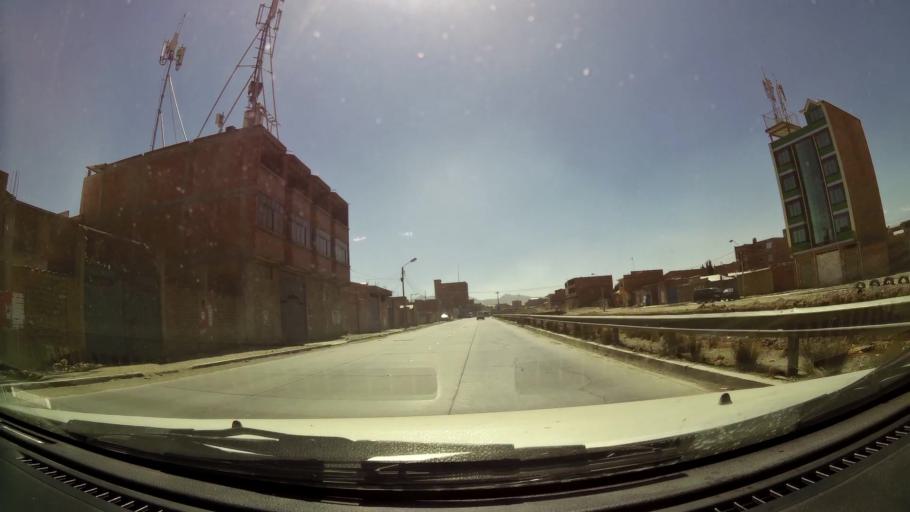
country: BO
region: La Paz
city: La Paz
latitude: -16.4960
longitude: -68.2059
